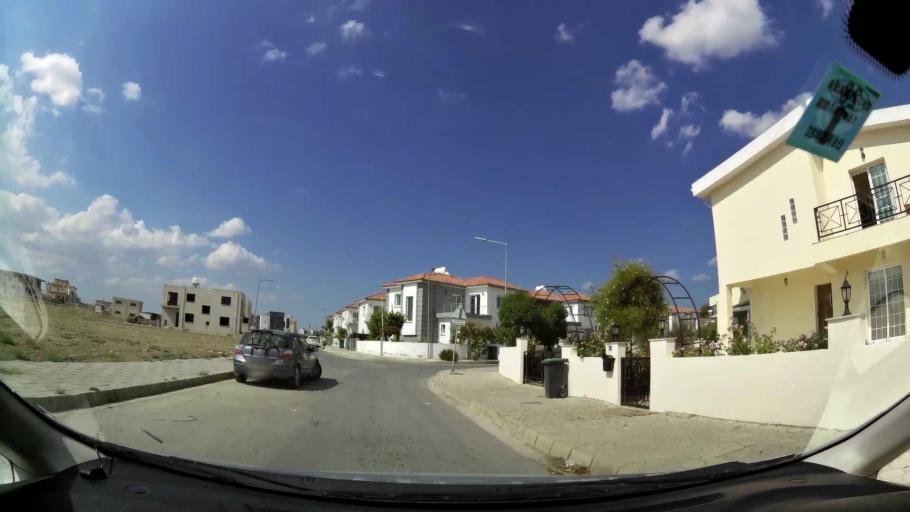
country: CY
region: Lefkosia
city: Nicosia
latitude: 35.2214
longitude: 33.2946
